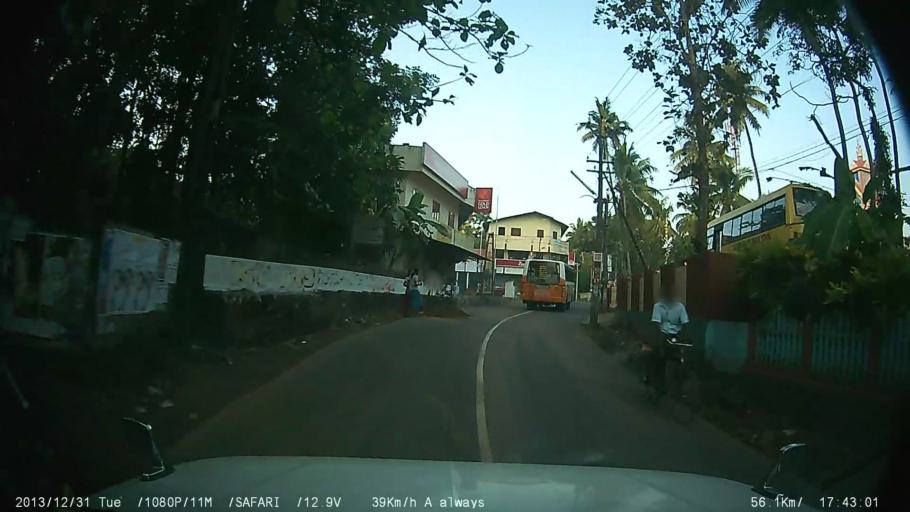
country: IN
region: Kerala
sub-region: Kottayam
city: Vaikam
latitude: 9.7201
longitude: 76.4765
